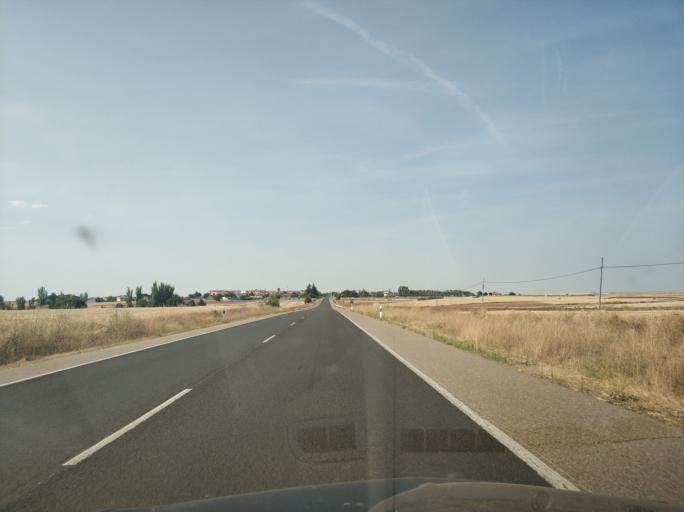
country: ES
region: Castille and Leon
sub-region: Provincia de Salamanca
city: Villares de la Reina
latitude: 41.0103
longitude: -5.6688
